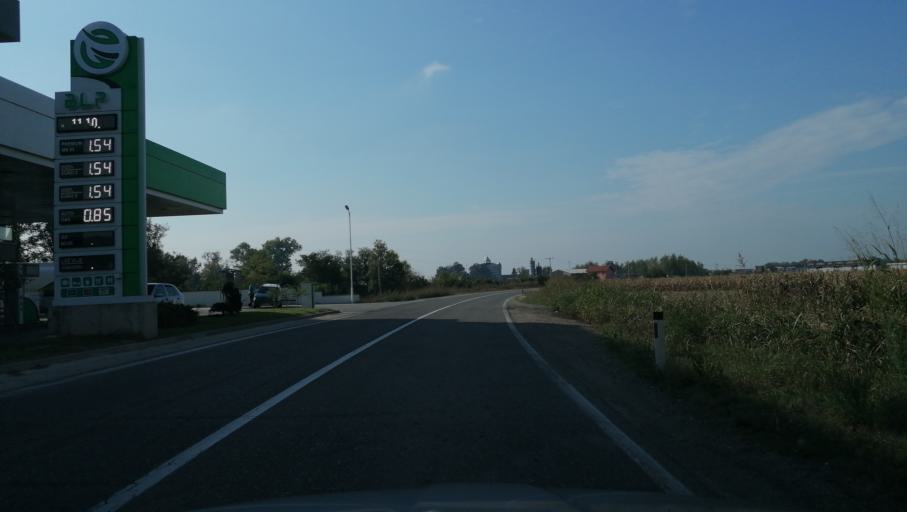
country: BA
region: Republika Srpska
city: Popovi
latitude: 44.7816
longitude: 19.2877
